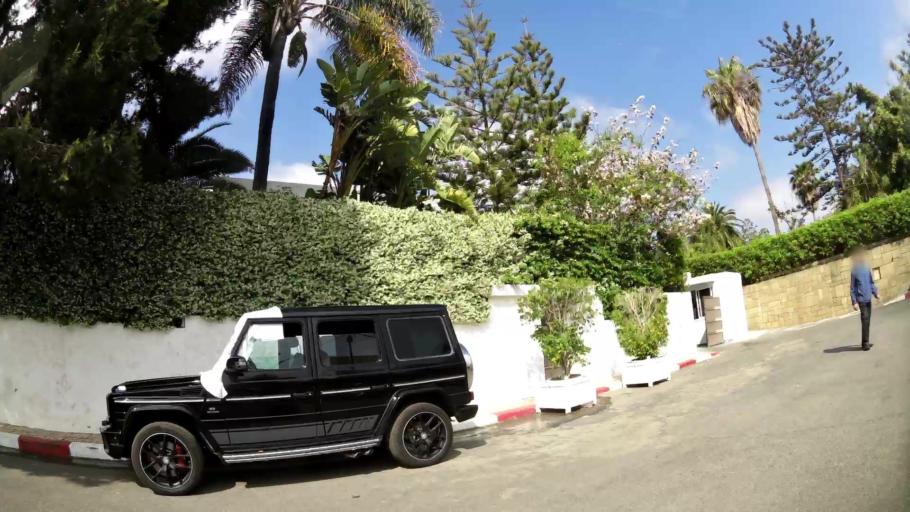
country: MA
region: Rabat-Sale-Zemmour-Zaer
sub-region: Rabat
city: Rabat
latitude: 33.9758
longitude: -6.8415
